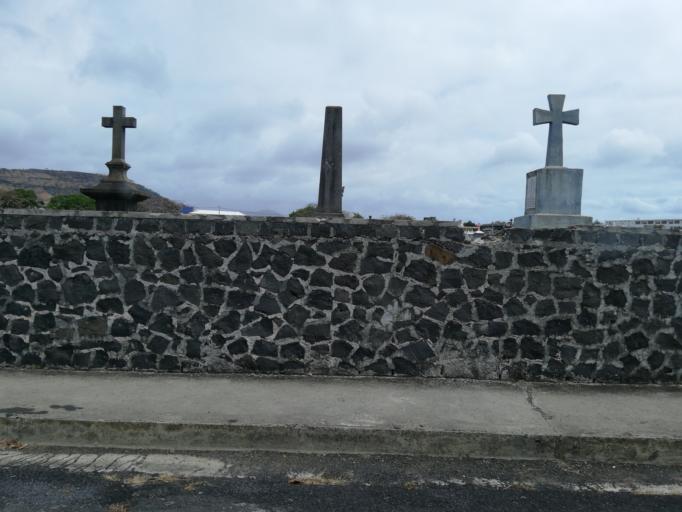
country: MU
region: Port Louis
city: Port Louis
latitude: -20.1617
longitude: 57.4864
